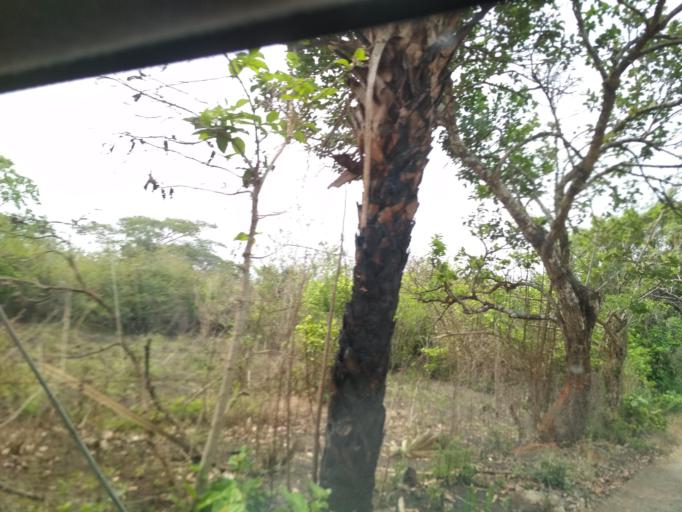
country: MX
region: Veracruz
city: Paso del Toro
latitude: 19.0249
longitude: -96.1411
